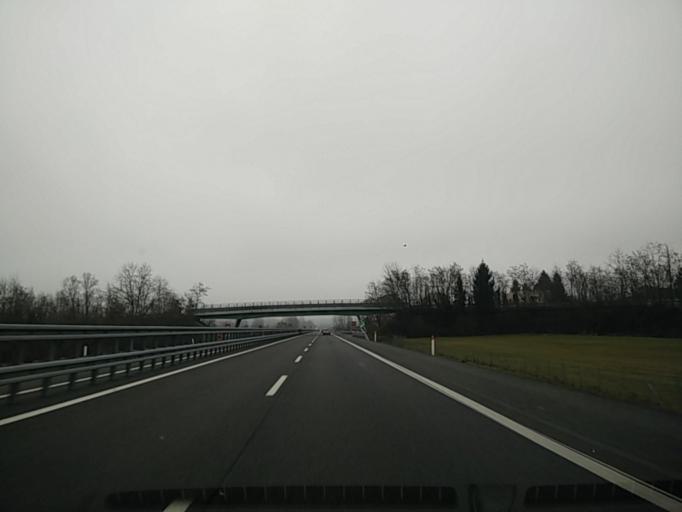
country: IT
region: Piedmont
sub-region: Provincia di Asti
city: Villafranca d'Asti
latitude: 44.9166
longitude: 8.0338
